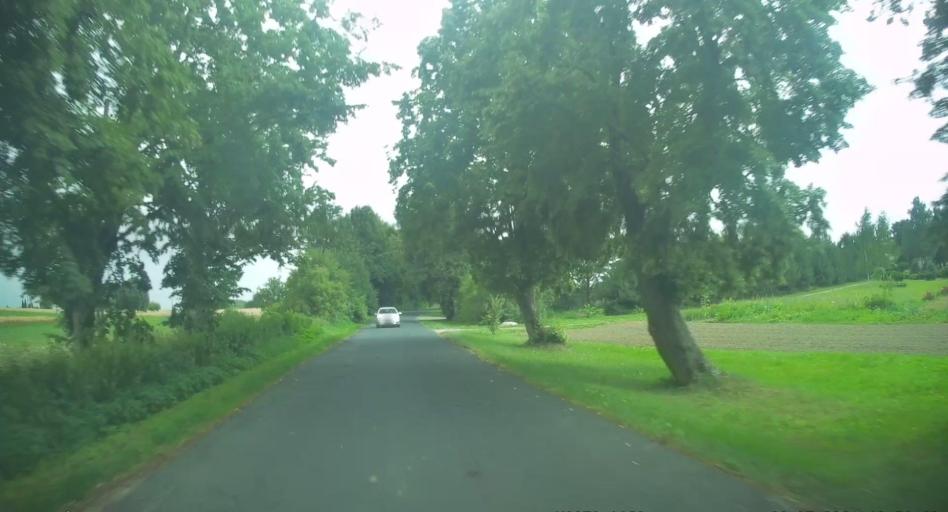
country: PL
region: Lodz Voivodeship
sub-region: Powiat rawski
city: Rawa Mazowiecka
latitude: 51.7701
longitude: 20.1831
